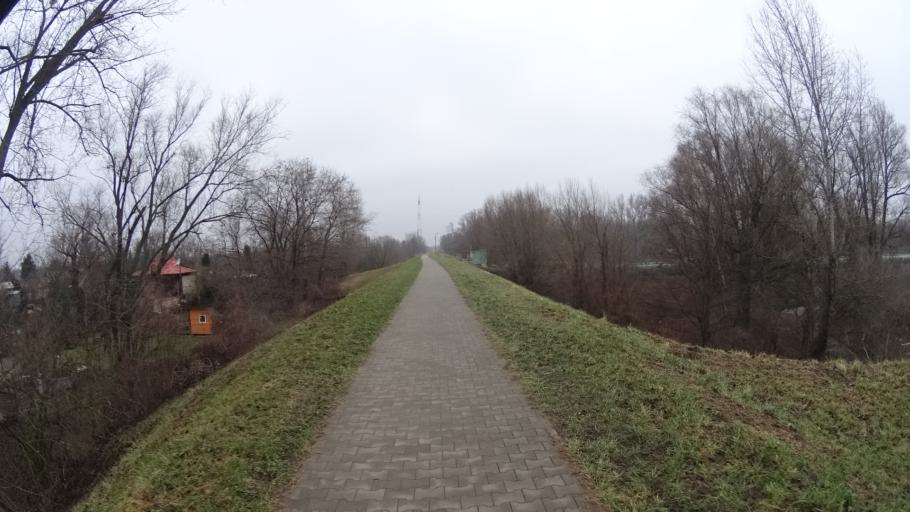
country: PL
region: Masovian Voivodeship
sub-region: Warszawa
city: Wilanow
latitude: 52.1920
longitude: 21.1020
